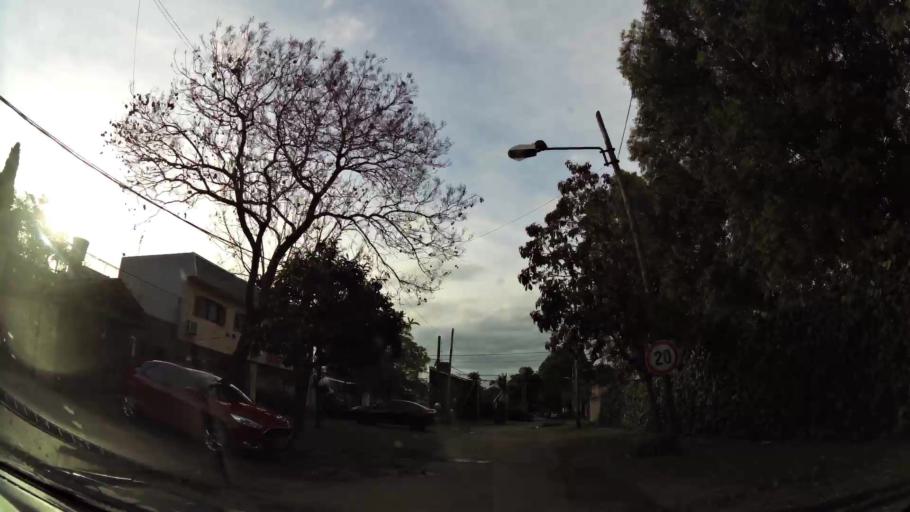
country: AR
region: Buenos Aires
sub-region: Partido de Quilmes
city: Quilmes
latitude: -34.7260
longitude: -58.2454
